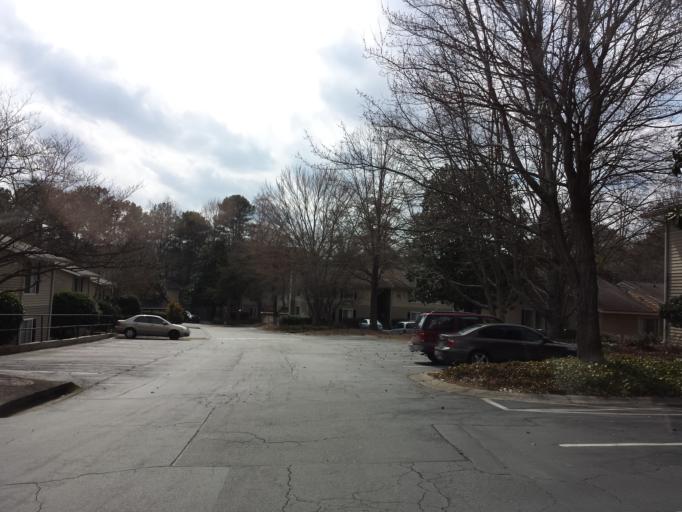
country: US
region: Georgia
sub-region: Cobb County
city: Vinings
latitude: 33.9073
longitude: -84.4697
